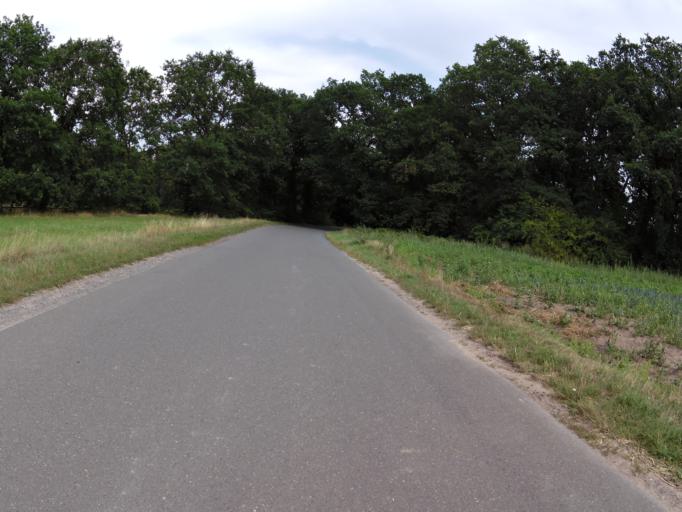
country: DE
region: Lower Saxony
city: Nienburg
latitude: 52.6083
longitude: 9.1914
